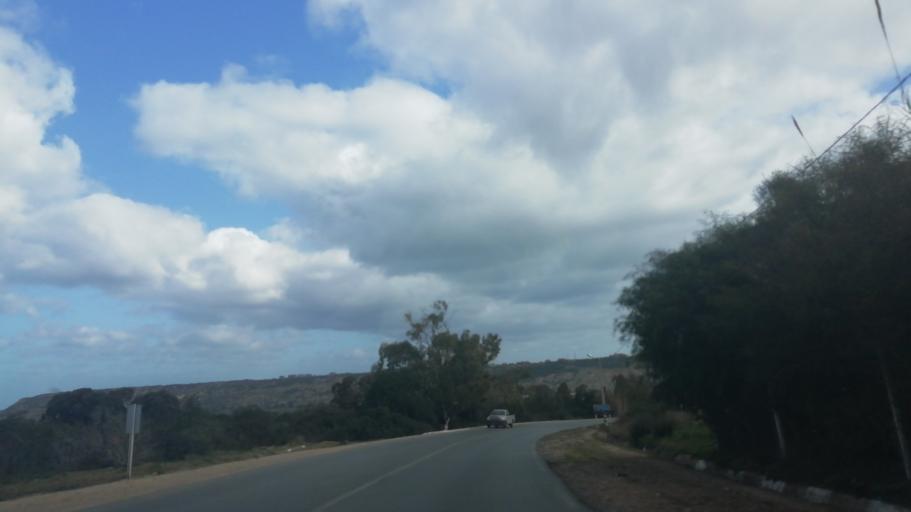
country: DZ
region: Relizane
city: Mazouna
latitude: 36.2944
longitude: 0.6562
